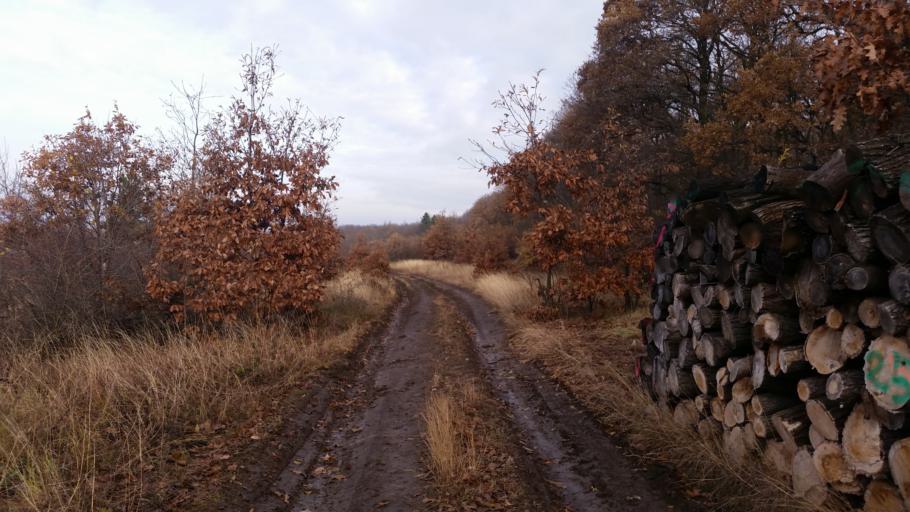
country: HU
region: Pest
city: Telki
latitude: 47.5703
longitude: 18.8178
